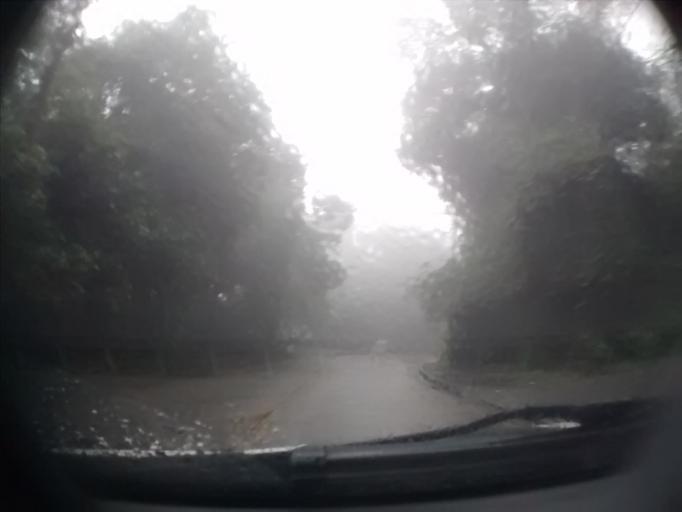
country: BR
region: Rio de Janeiro
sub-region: Rio De Janeiro
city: Rio de Janeiro
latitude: -22.9871
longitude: -43.2704
